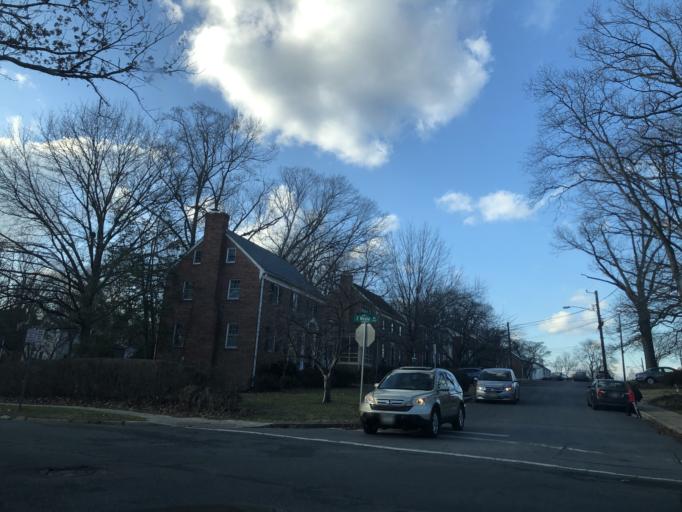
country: US
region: Maryland
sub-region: Montgomery County
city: Four Corners
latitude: 39.0035
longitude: -77.0033
